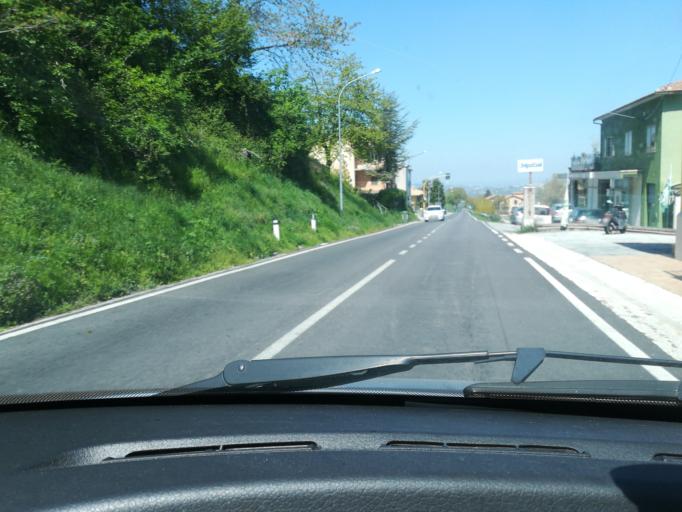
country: IT
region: The Marches
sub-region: Provincia di Macerata
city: Cingoli
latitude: 43.3750
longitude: 13.2187
